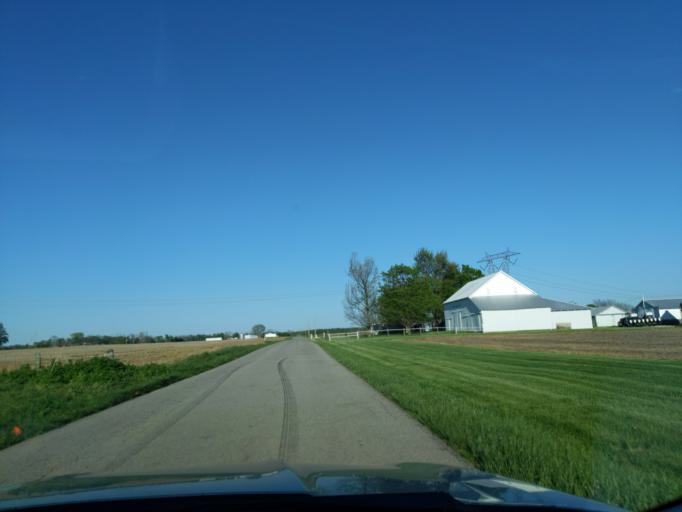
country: US
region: Indiana
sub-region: Decatur County
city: Westport
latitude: 39.1980
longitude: -85.5683
